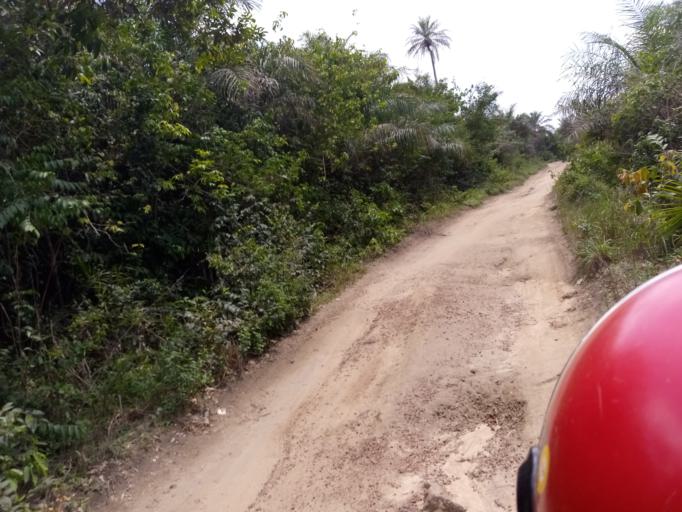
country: SL
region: Western Area
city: Waterloo
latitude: 8.3682
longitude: -13.0025
